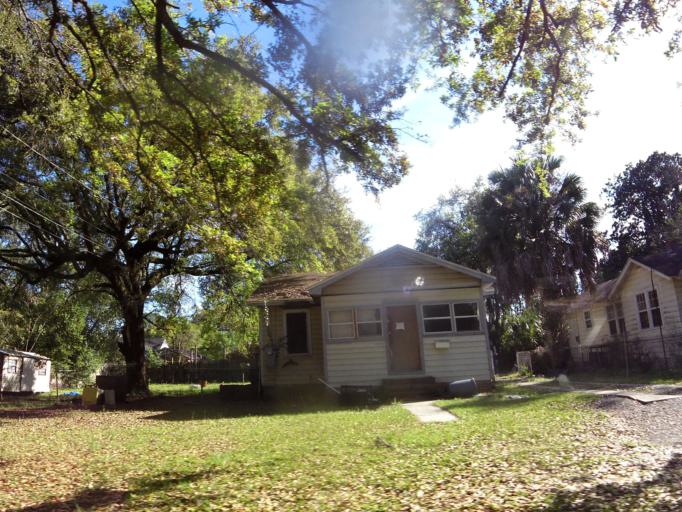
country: US
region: Florida
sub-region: Duval County
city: Jacksonville
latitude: 30.3748
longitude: -81.6475
